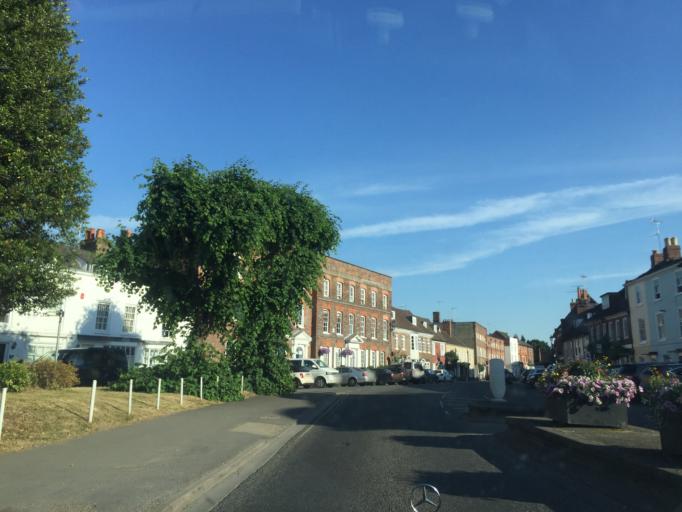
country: GB
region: England
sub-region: Oxfordshire
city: Henley on Thames
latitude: 51.5410
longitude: -0.9046
